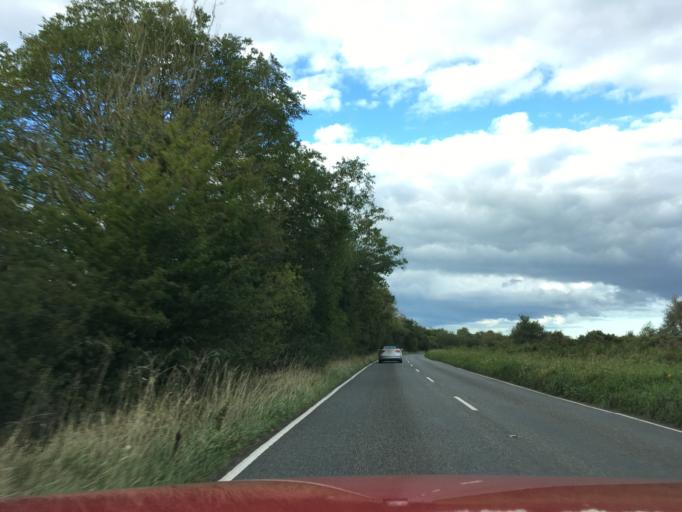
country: GB
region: England
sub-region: Devon
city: Honiton
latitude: 50.7647
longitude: -3.2132
